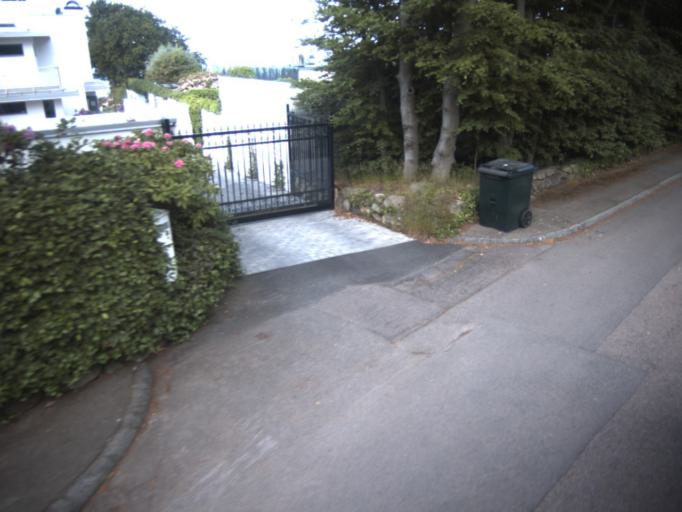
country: SE
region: Skane
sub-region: Helsingborg
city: Helsingborg
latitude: 56.0896
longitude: 12.6516
